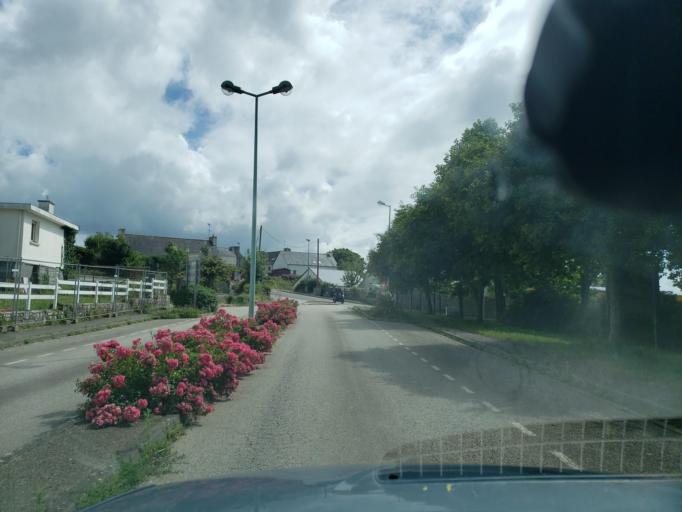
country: FR
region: Brittany
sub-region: Departement du Finistere
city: Ploneour-Lanvern
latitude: 47.9092
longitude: -4.2802
